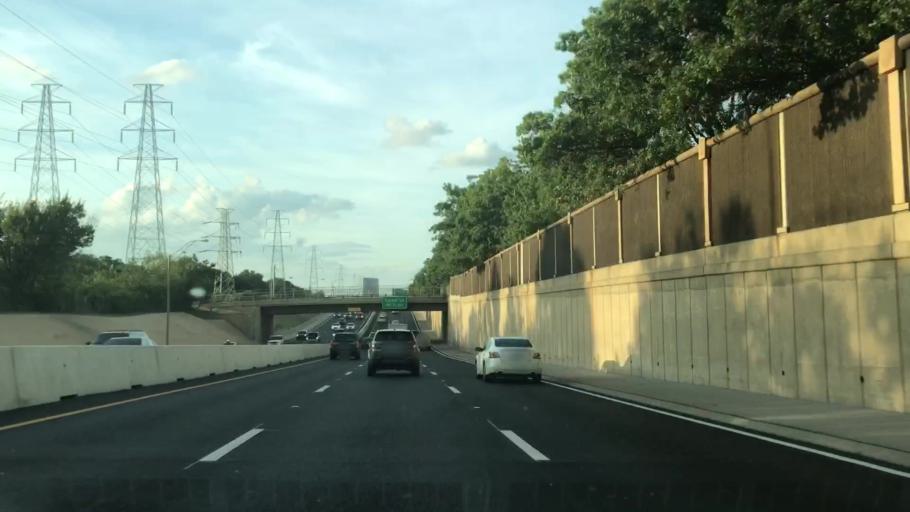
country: US
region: Texas
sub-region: Dallas County
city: University Park
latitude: 32.9012
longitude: -96.8116
